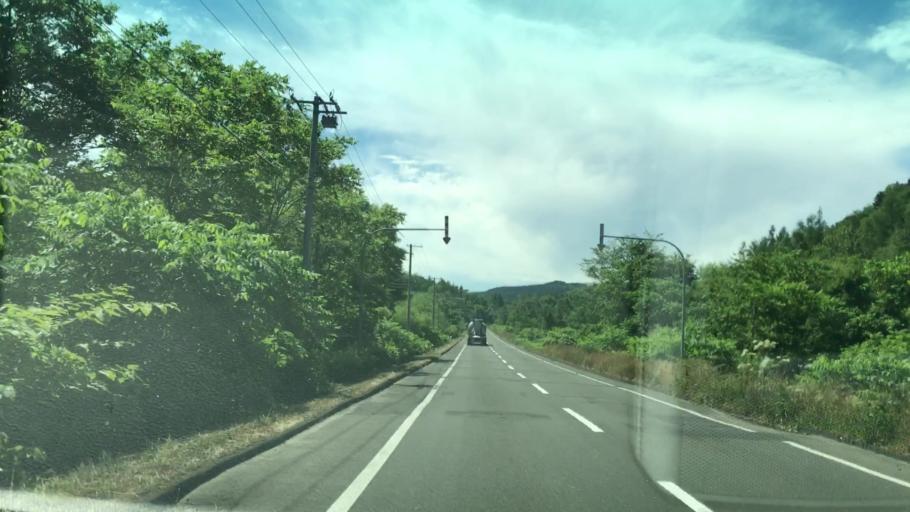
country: JP
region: Hokkaido
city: Shimo-furano
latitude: 42.9383
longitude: 142.4450
